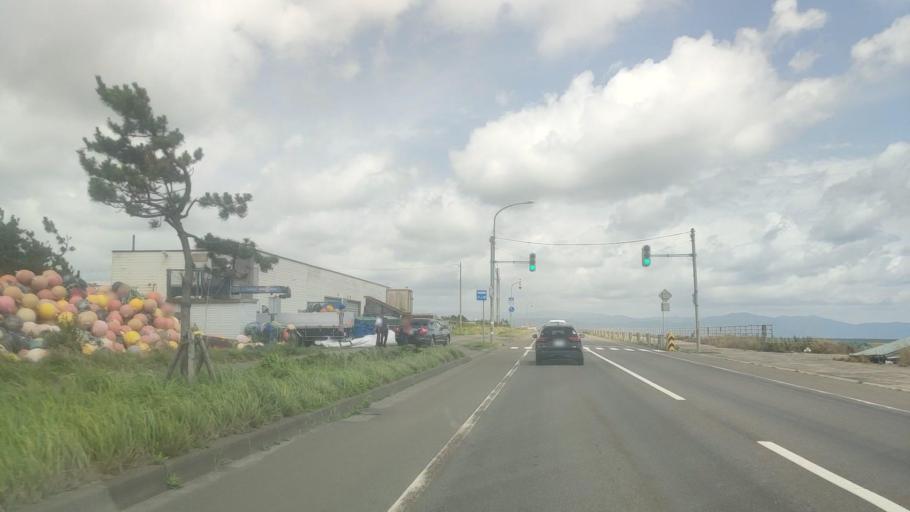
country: JP
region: Hokkaido
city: Niseko Town
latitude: 42.5023
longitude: 140.3708
